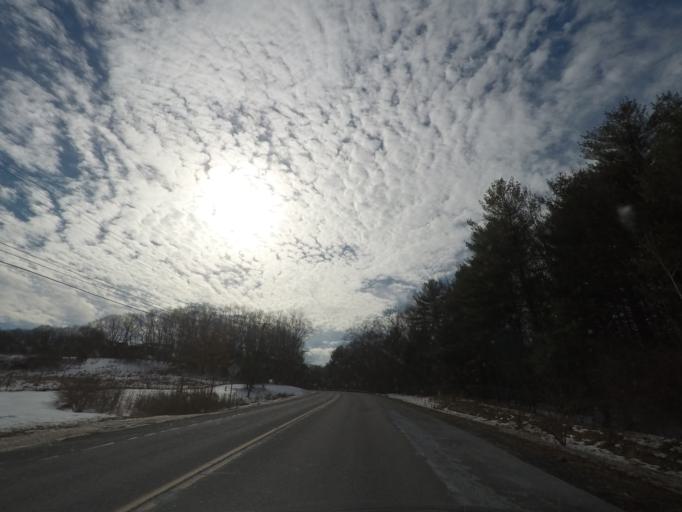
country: US
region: New York
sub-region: Albany County
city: Voorheesville
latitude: 42.6745
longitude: -73.9104
